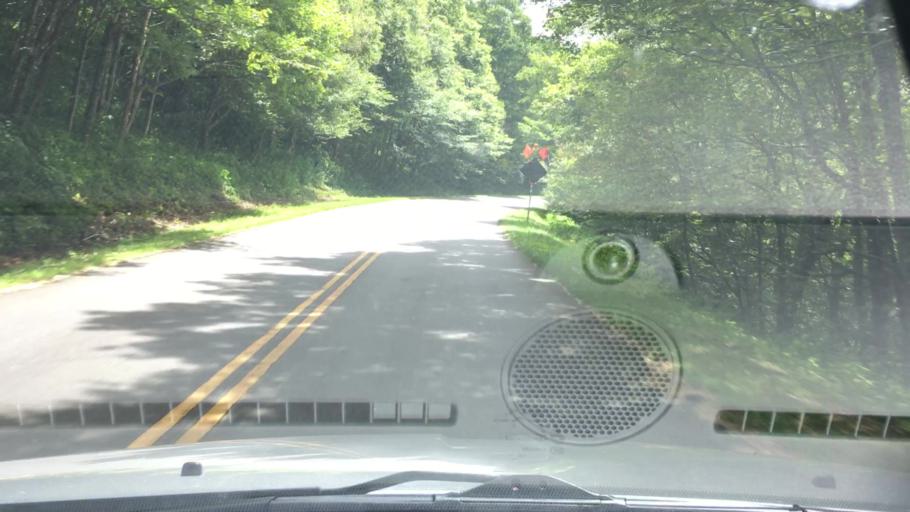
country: US
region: North Carolina
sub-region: Buncombe County
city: Swannanoa
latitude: 35.6904
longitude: -82.3900
